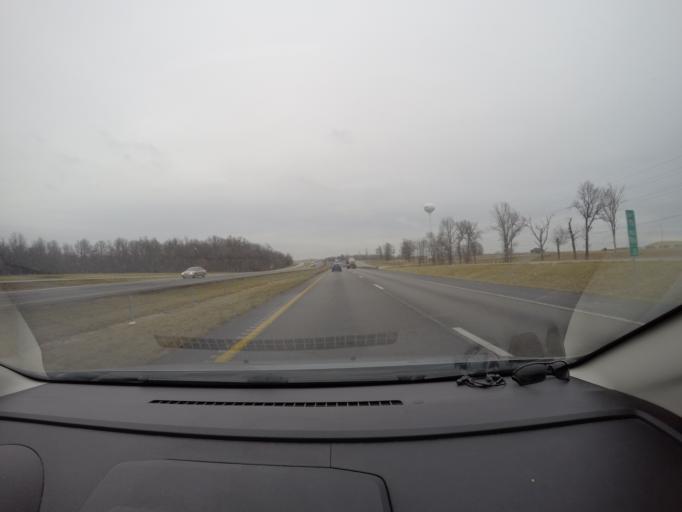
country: US
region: Missouri
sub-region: Warren County
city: Warrenton
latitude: 38.8466
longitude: -91.2692
